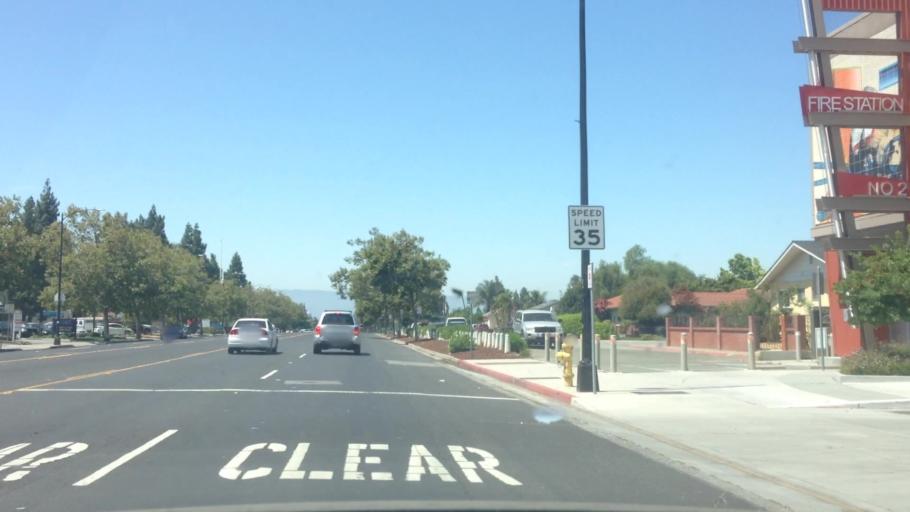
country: US
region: California
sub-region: Santa Clara County
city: Alum Rock
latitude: 37.3645
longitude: -121.8312
